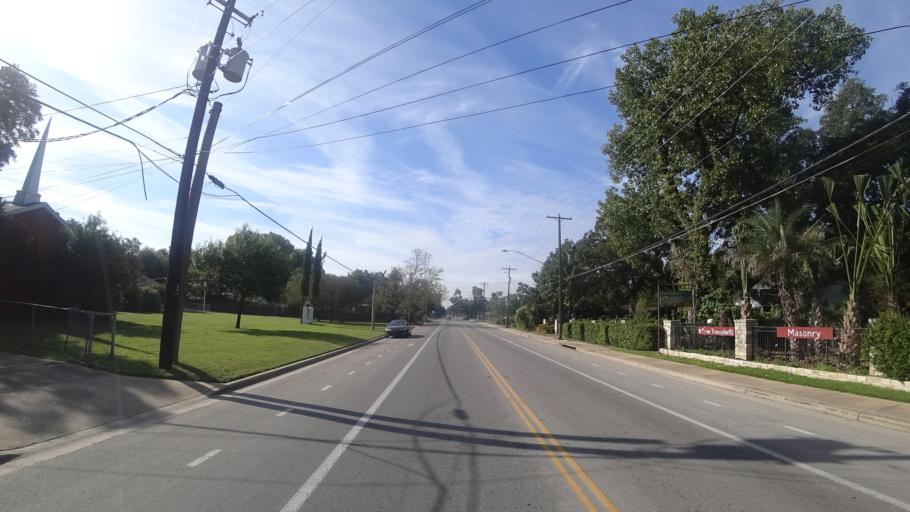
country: US
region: Texas
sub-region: Travis County
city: Austin
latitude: 30.2670
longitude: -97.7017
